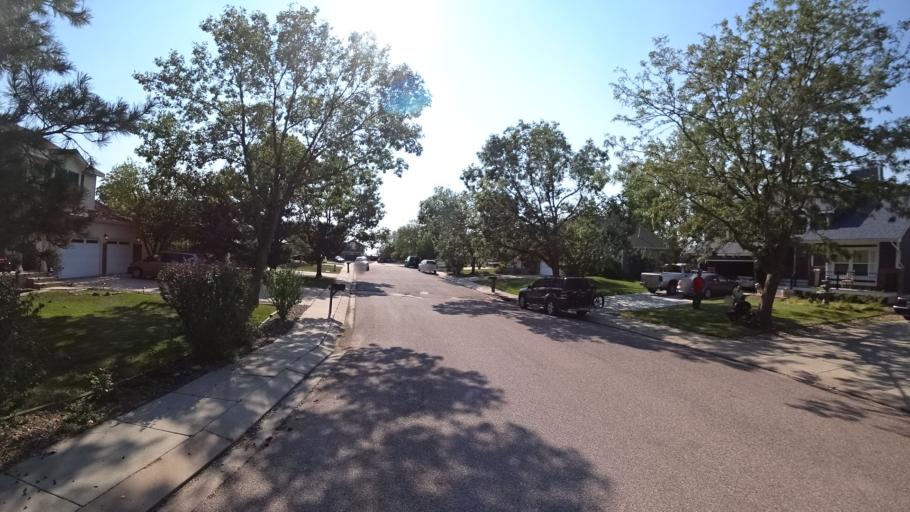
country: US
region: Colorado
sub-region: El Paso County
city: Stratmoor
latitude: 38.7788
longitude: -104.8023
